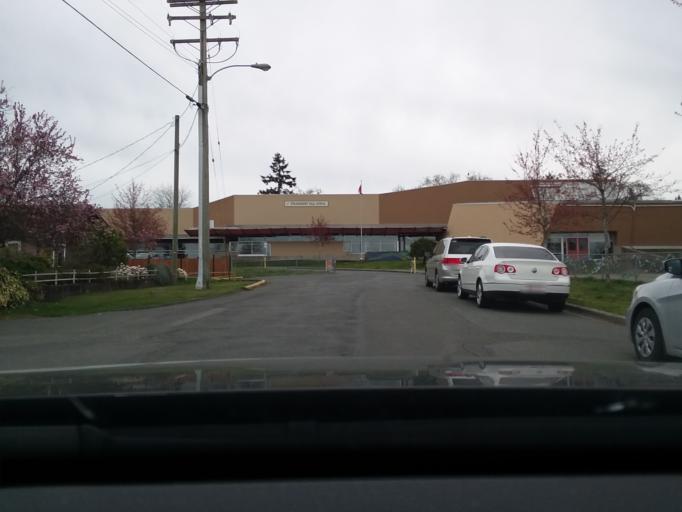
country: CA
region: British Columbia
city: Victoria
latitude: 48.4784
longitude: -123.4171
